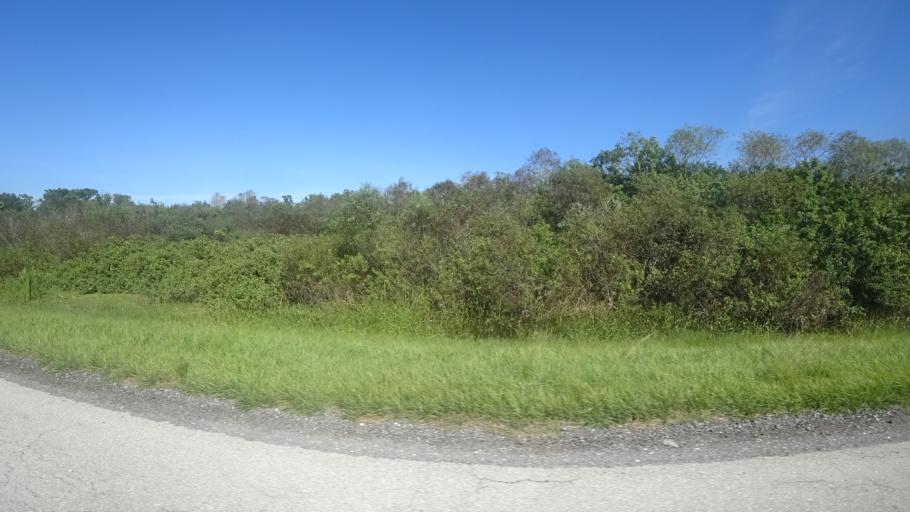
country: US
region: Florida
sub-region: Sarasota County
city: Warm Mineral Springs
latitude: 27.2736
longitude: -82.1407
